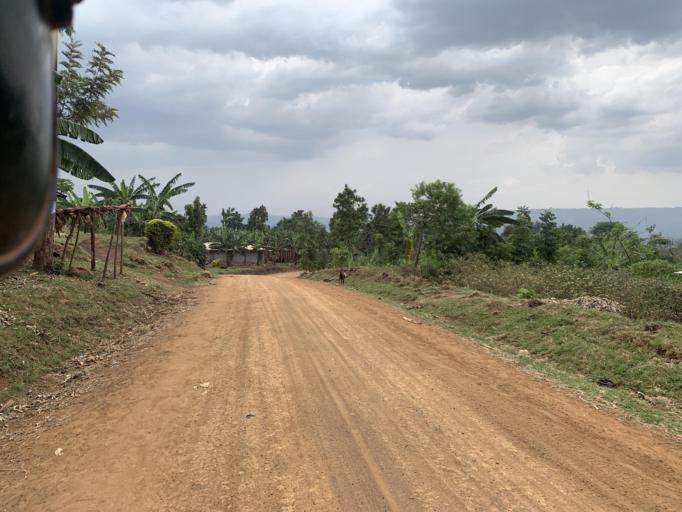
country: UG
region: Eastern Region
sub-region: Sironko District
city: Sironko
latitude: 1.2559
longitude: 34.2922
